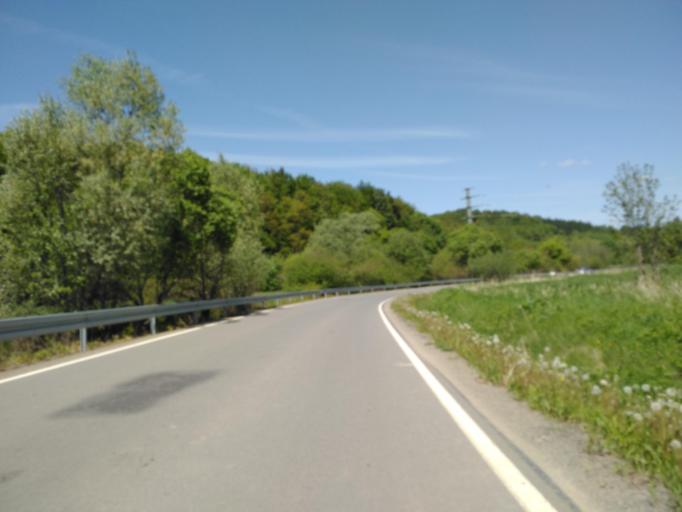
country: PL
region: Subcarpathian Voivodeship
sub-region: Powiat krosnienski
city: Dukla
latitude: 49.5806
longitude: 21.6943
